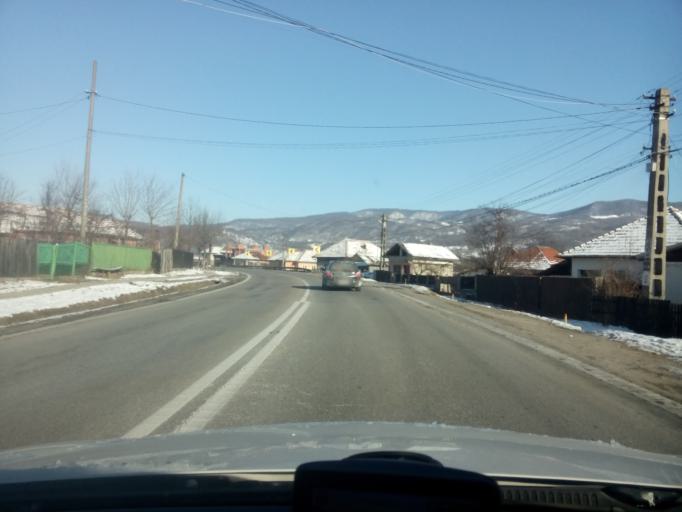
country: RO
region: Valcea
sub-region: Comuna Daesti
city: Daesti
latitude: 45.1916
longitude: 24.3735
